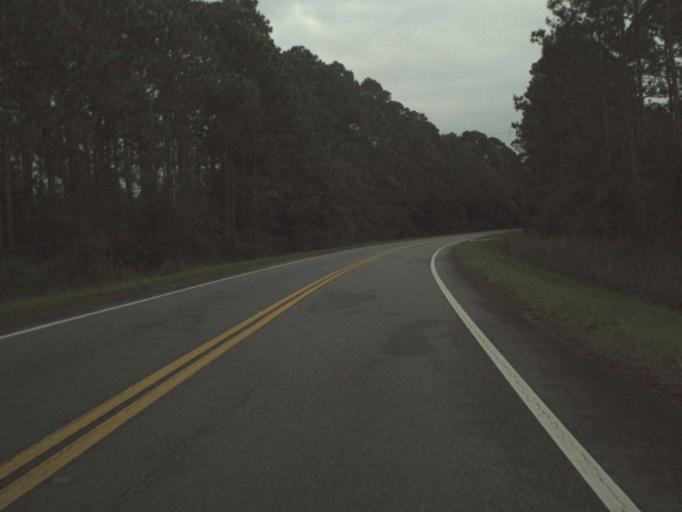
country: US
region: Florida
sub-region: Franklin County
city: Eastpoint
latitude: 29.8278
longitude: -84.8590
